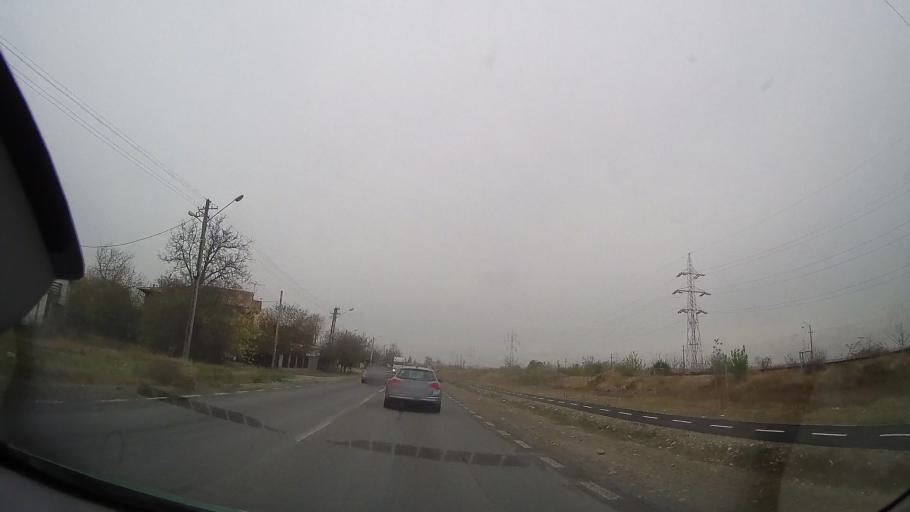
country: RO
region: Prahova
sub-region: Comuna Blejoiu
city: Ploiestiori
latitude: 44.9821
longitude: 26.0162
